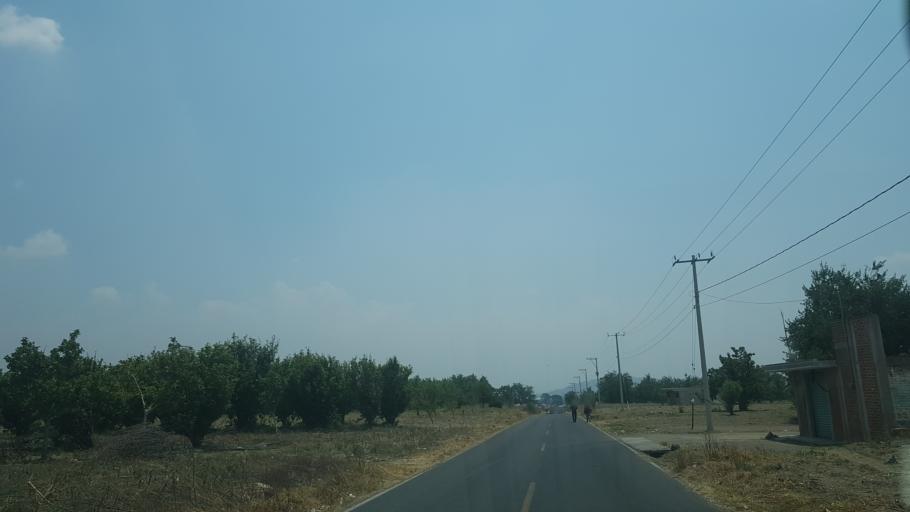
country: MX
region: Puebla
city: San Andres Calpan
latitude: 19.0976
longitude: -98.4186
